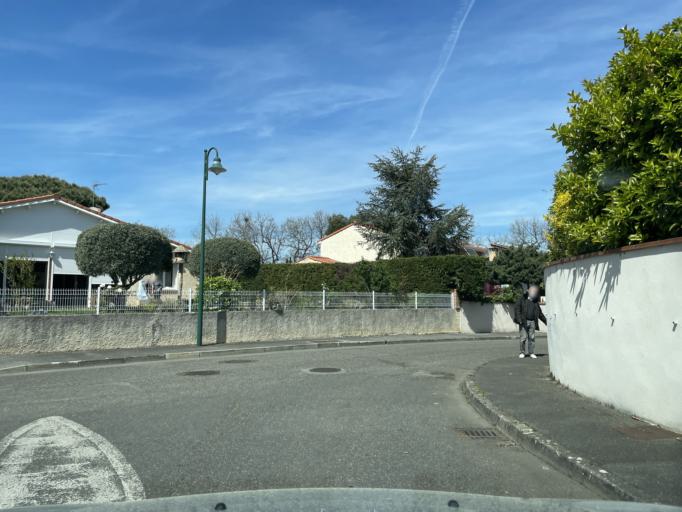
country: FR
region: Midi-Pyrenees
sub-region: Departement de la Haute-Garonne
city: Pibrac
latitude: 43.6168
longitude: 1.2690
